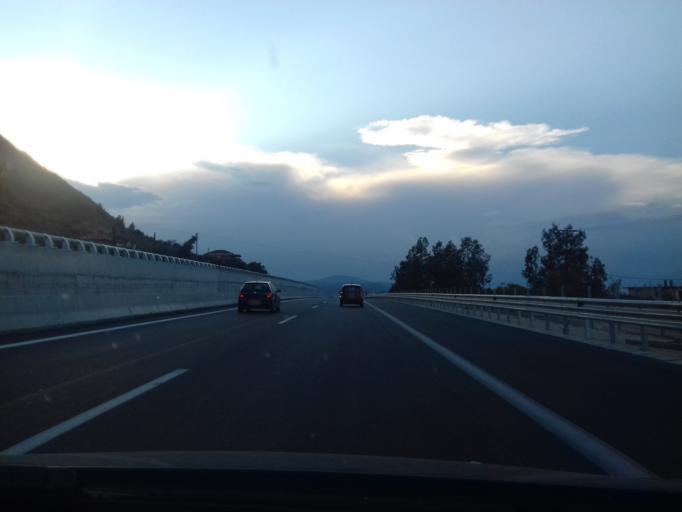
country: GR
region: West Greece
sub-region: Nomos Achaias
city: Temeni
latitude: 38.2117
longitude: 22.1255
